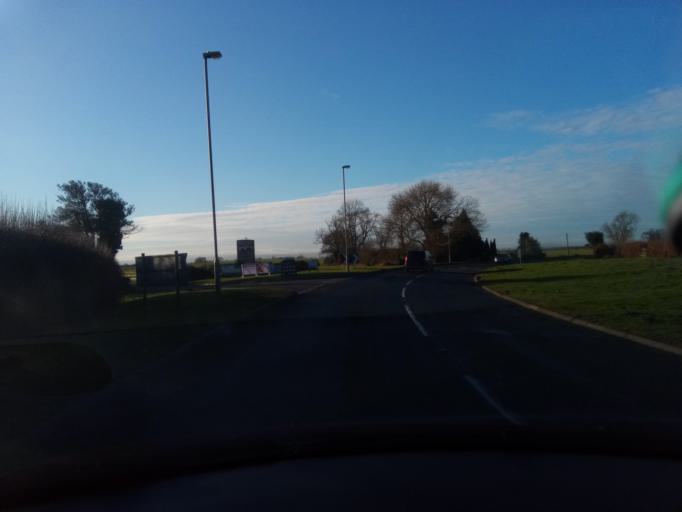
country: GB
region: England
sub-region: North Yorkshire
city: Thirsk
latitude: 54.2221
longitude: -1.4014
